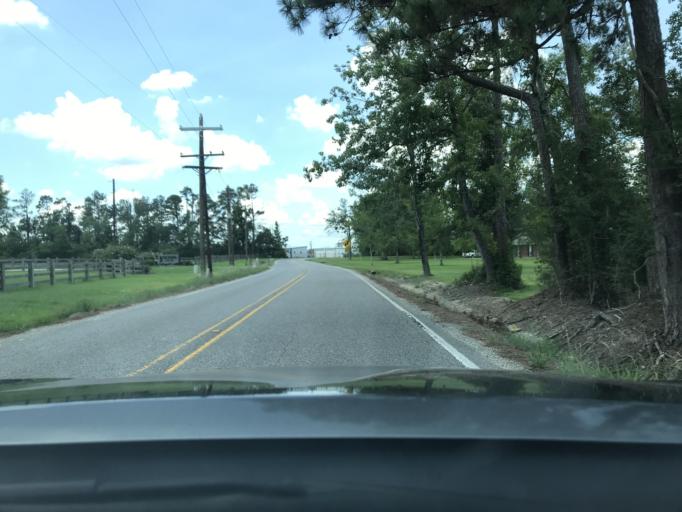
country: US
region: Louisiana
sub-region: Calcasieu Parish
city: Moss Bluff
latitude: 30.3274
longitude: -93.1707
